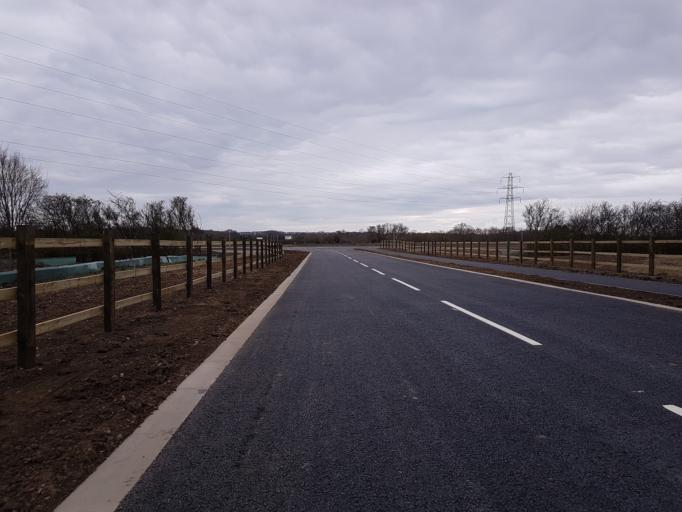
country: GB
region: England
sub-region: Cambridgeshire
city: Girton
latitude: 52.2410
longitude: 0.0482
